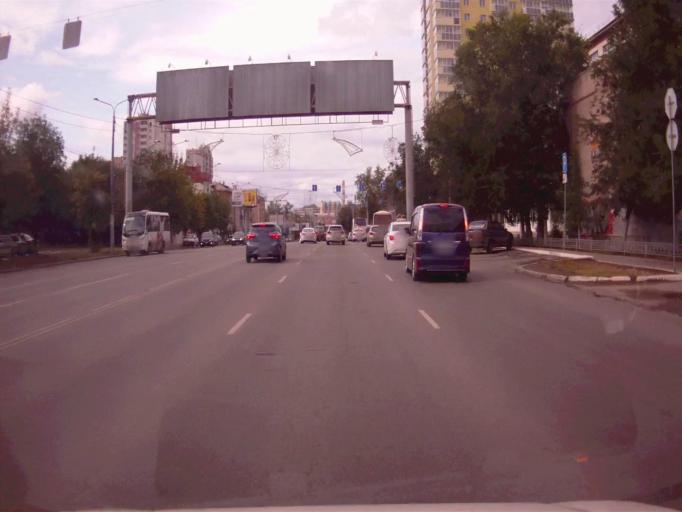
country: RU
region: Chelyabinsk
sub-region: Gorod Chelyabinsk
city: Chelyabinsk
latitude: 55.1438
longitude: 61.3885
